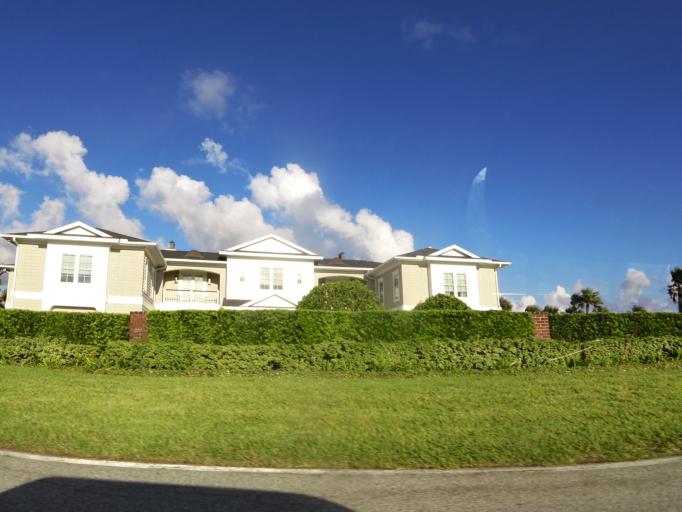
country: US
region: Florida
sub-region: Saint Johns County
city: Sawgrass
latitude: 30.1988
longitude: -81.3667
